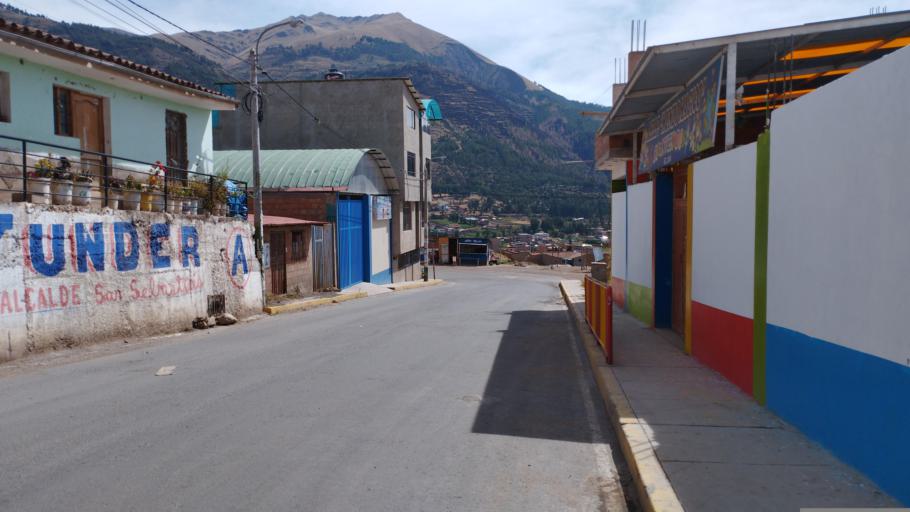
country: PE
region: Cusco
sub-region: Provincia de Cusco
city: Cusco
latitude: -13.5223
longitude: -71.9145
